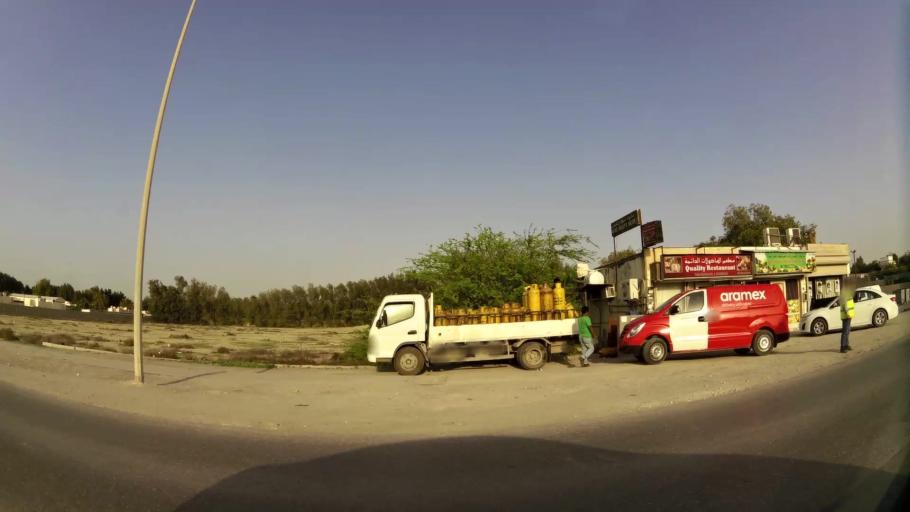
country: BH
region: Manama
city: Jidd Hafs
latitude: 26.1984
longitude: 50.4854
